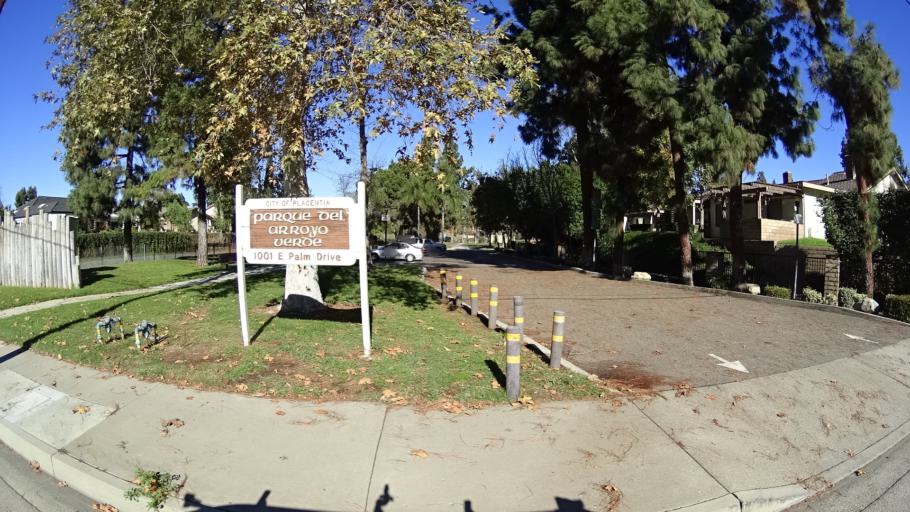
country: US
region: California
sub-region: Orange County
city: Placentia
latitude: 33.8833
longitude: -117.8469
